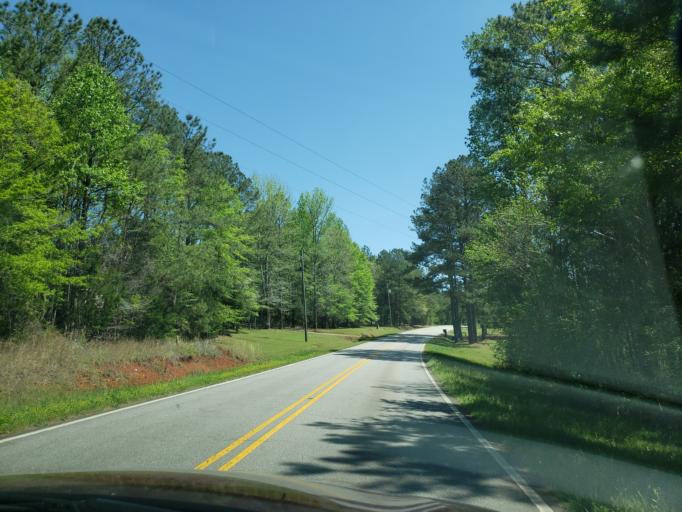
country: US
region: Alabama
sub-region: Tallapoosa County
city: Camp Hill
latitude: 32.7024
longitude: -85.7107
